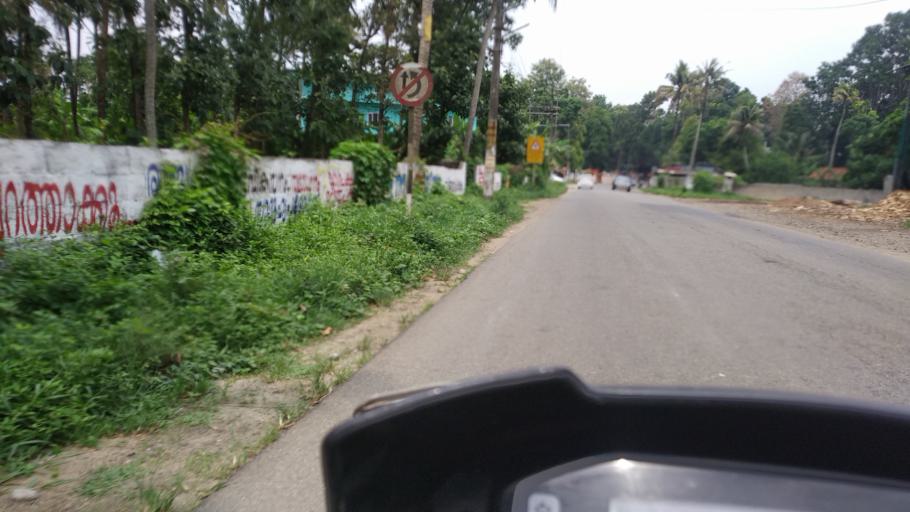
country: IN
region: Kerala
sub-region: Ernakulam
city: Perumpavur
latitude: 10.1092
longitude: 76.5353
